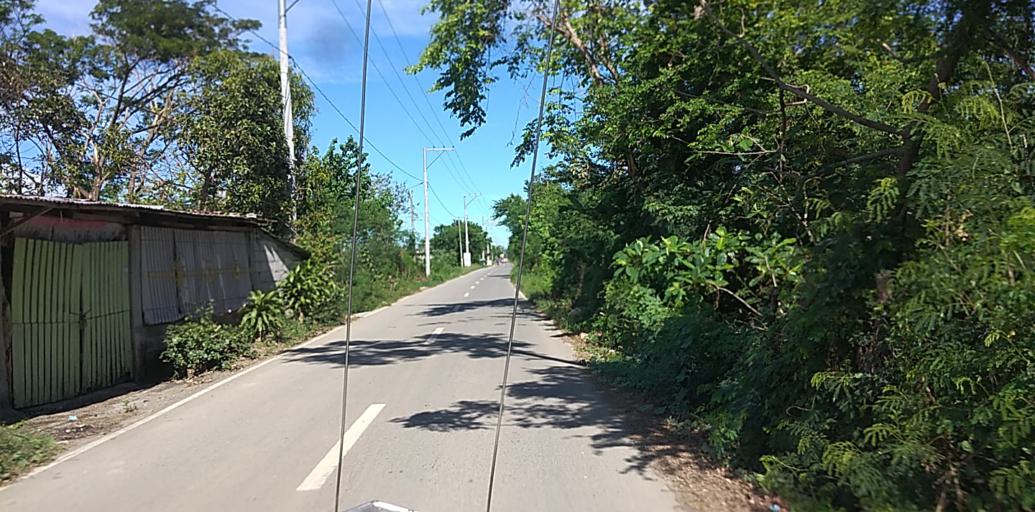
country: PH
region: Central Luzon
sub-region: Province of Pampanga
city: Candaba
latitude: 15.1145
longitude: 120.8152
